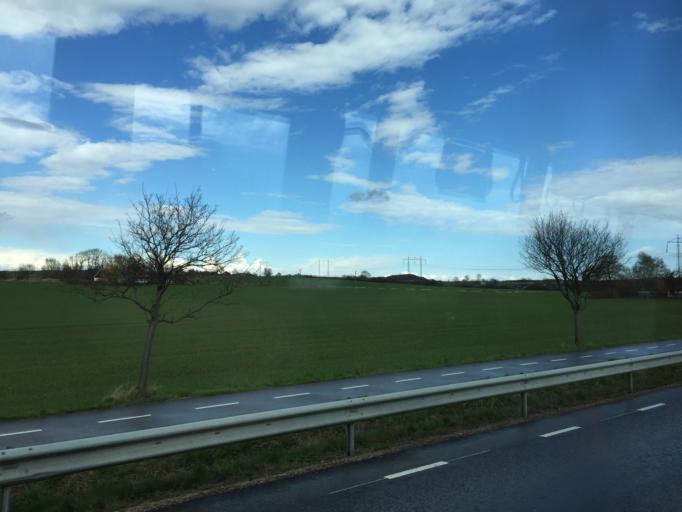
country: SE
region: Skane
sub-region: Staffanstorps Kommun
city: Staffanstorp
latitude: 55.6812
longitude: 13.2787
